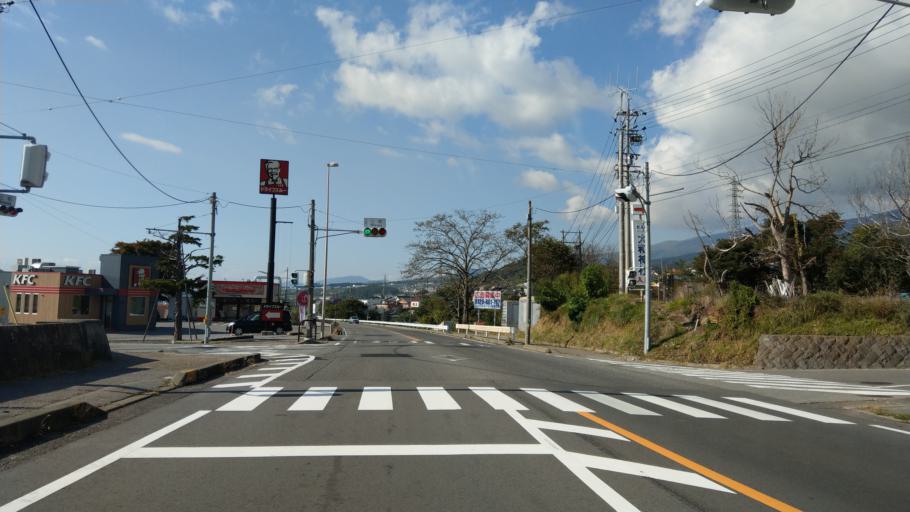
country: JP
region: Nagano
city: Komoro
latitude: 36.3312
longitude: 138.4309
